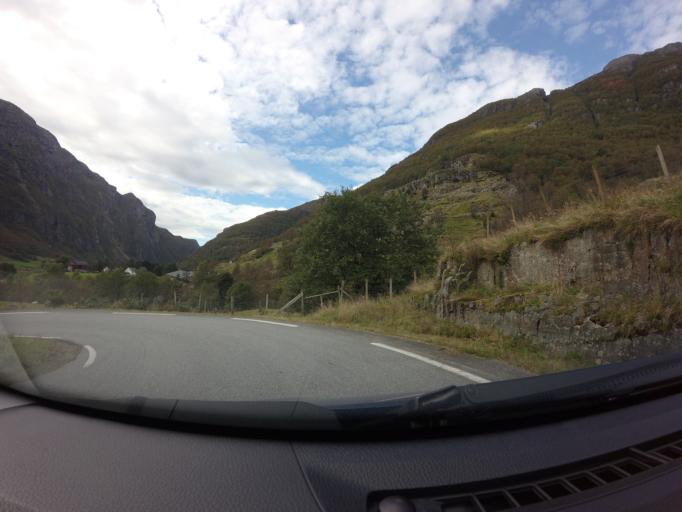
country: NO
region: Rogaland
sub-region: Forsand
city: Forsand
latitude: 58.8483
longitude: 6.3634
